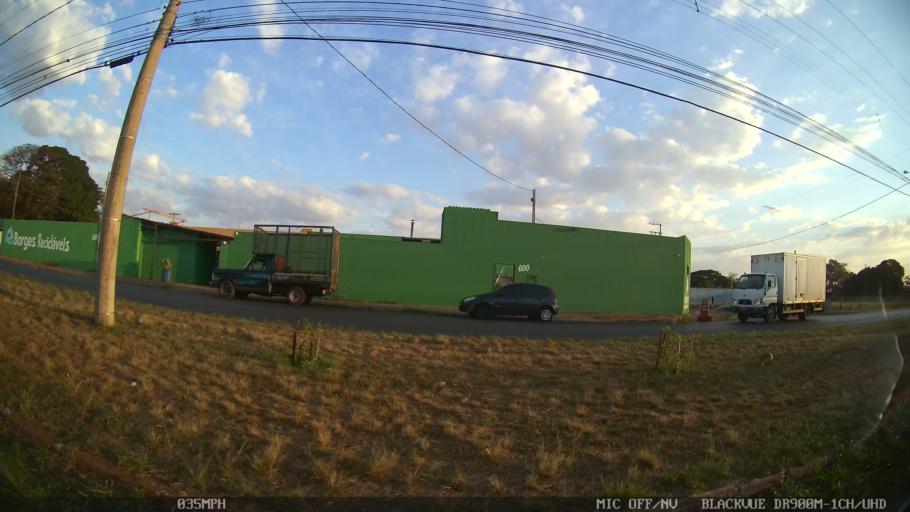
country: BR
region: Sao Paulo
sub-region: Ribeirao Preto
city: Ribeirao Preto
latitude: -21.1507
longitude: -47.7659
